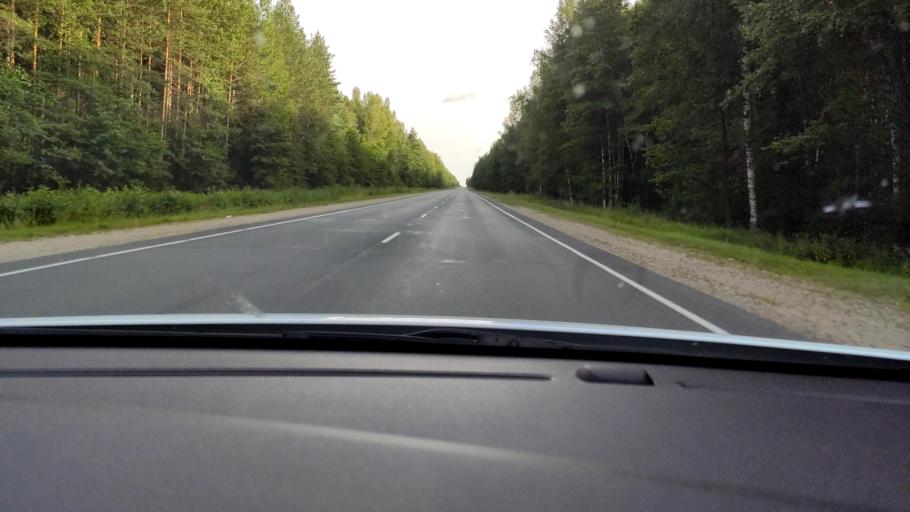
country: RU
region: Mariy-El
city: Suslonger
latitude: 56.2697
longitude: 48.2330
